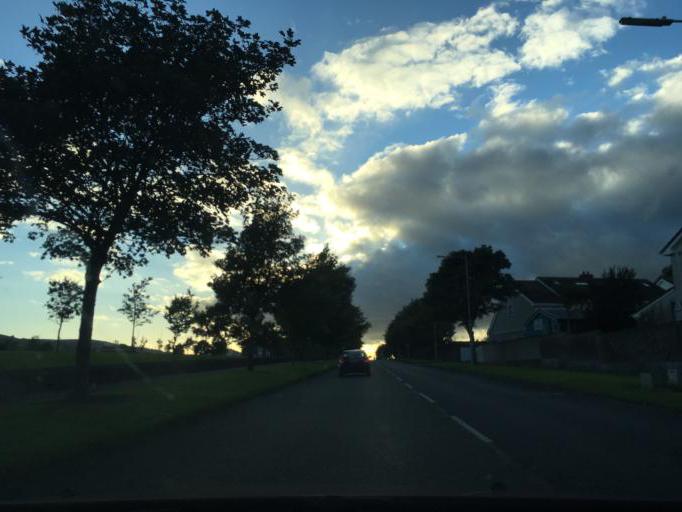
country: IE
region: Leinster
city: Oldbawn
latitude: 53.2766
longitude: -6.3605
